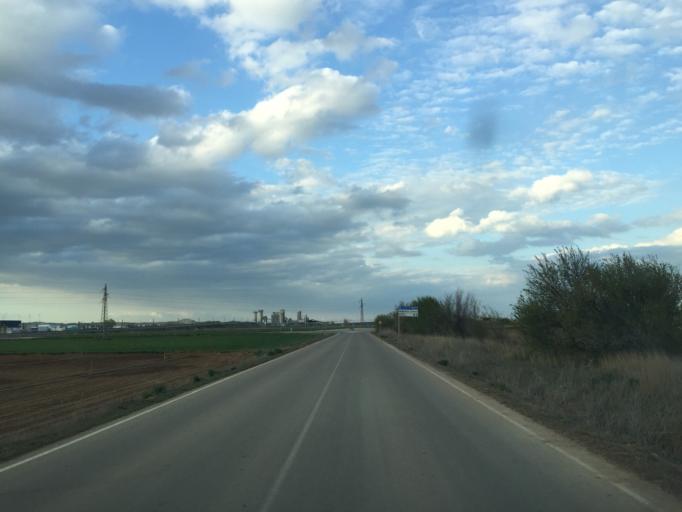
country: ES
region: Castille and Leon
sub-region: Provincia de Palencia
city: Venta de Banos
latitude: 41.9246
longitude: -4.4816
